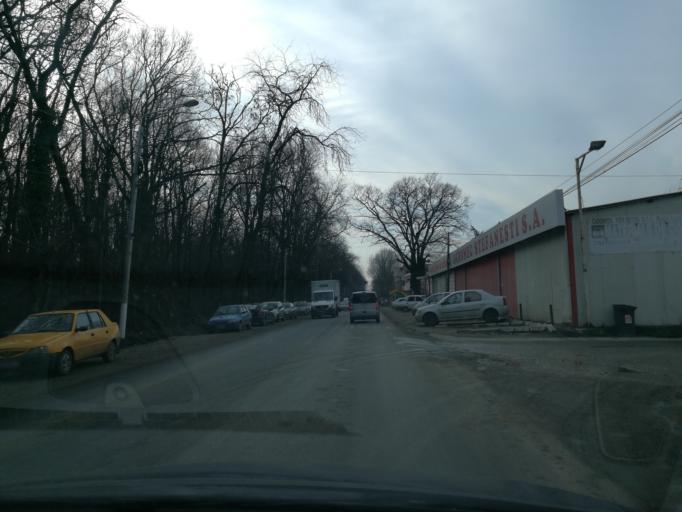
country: RO
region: Ilfov
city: Stefanestii de Jos
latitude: 44.5201
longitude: 26.1937
